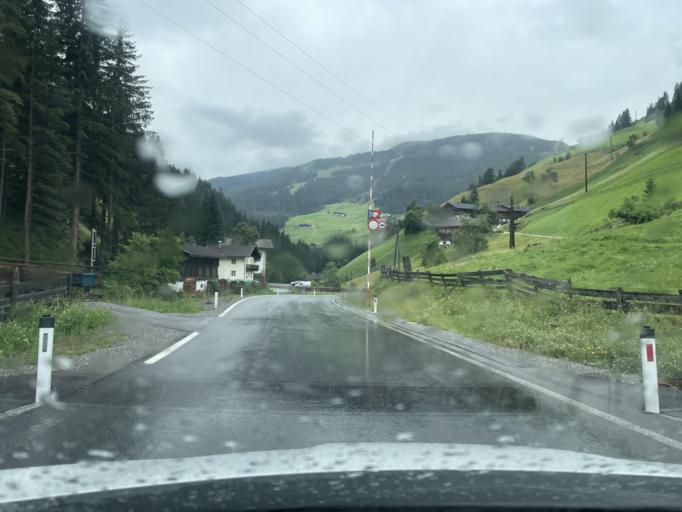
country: AT
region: Tyrol
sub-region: Politischer Bezirk Lienz
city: Ausservillgraten
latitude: 46.7912
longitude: 12.4396
